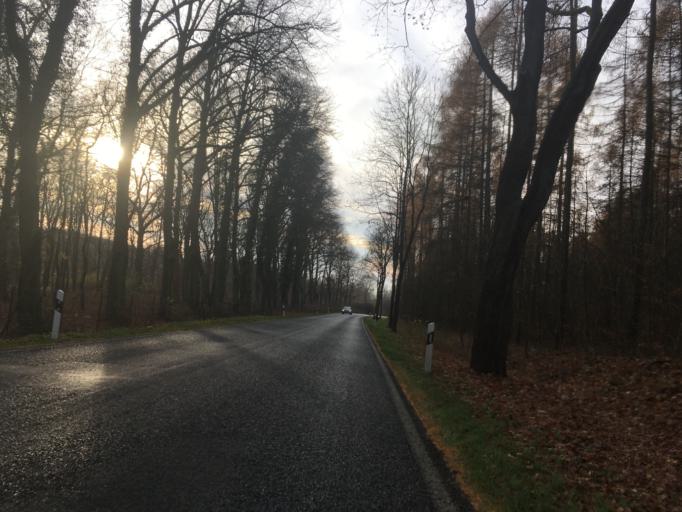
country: DE
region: Brandenburg
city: Eberswalde
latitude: 52.8479
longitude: 13.8443
